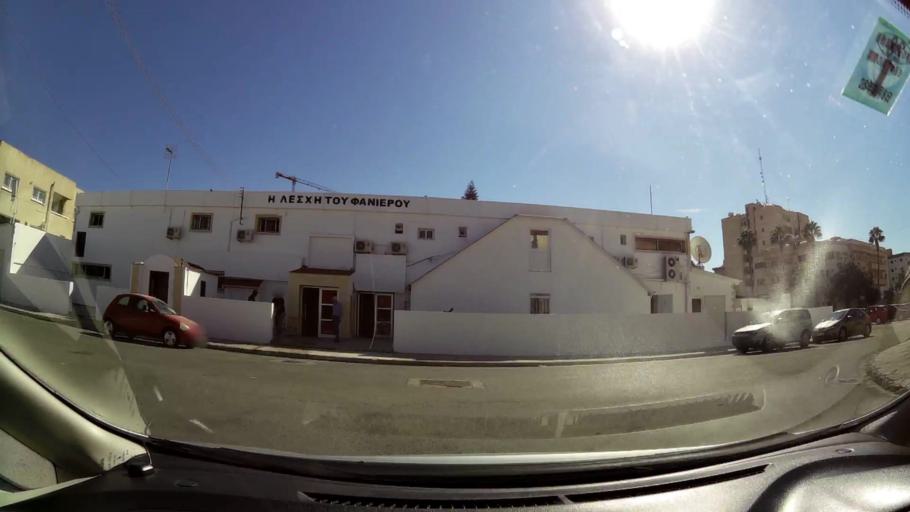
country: CY
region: Larnaka
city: Larnaca
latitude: 34.9315
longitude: 33.6349
